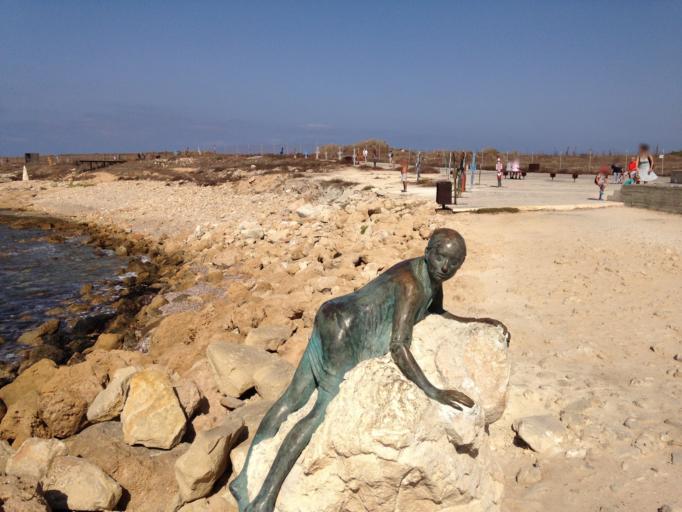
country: CY
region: Pafos
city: Paphos
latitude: 34.7540
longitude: 32.4066
